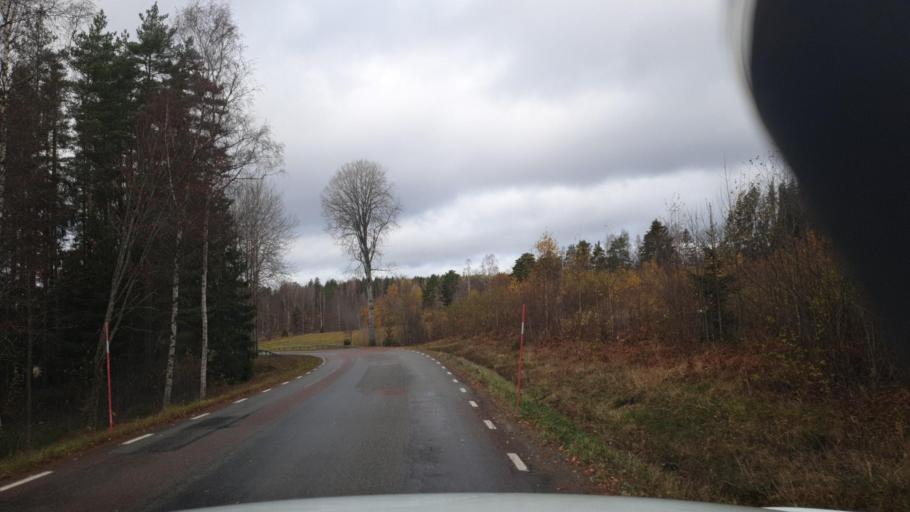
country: SE
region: Vaermland
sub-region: Arvika Kommun
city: Arvika
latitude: 59.5382
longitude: 12.7833
